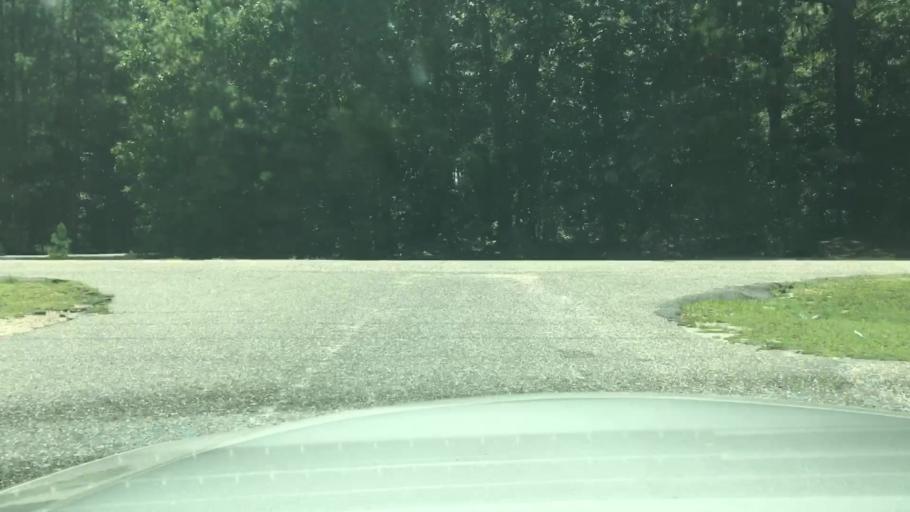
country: US
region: North Carolina
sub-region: Cumberland County
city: Hope Mills
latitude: 35.0113
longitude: -78.9683
